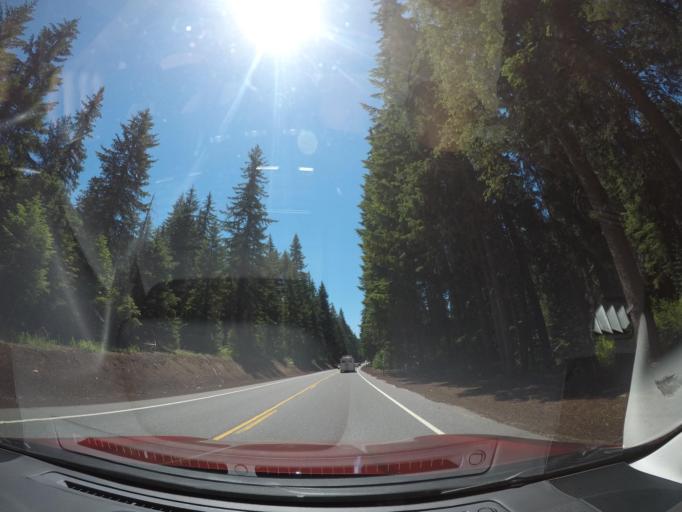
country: US
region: Oregon
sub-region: Deschutes County
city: Sisters
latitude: 44.5392
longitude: -121.9952
